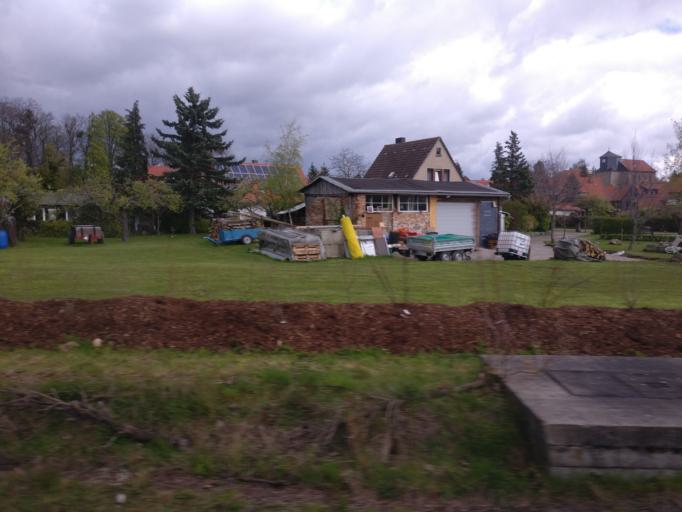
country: DE
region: Saxony-Anhalt
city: Darlingerode
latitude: 51.8499
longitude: 10.7312
